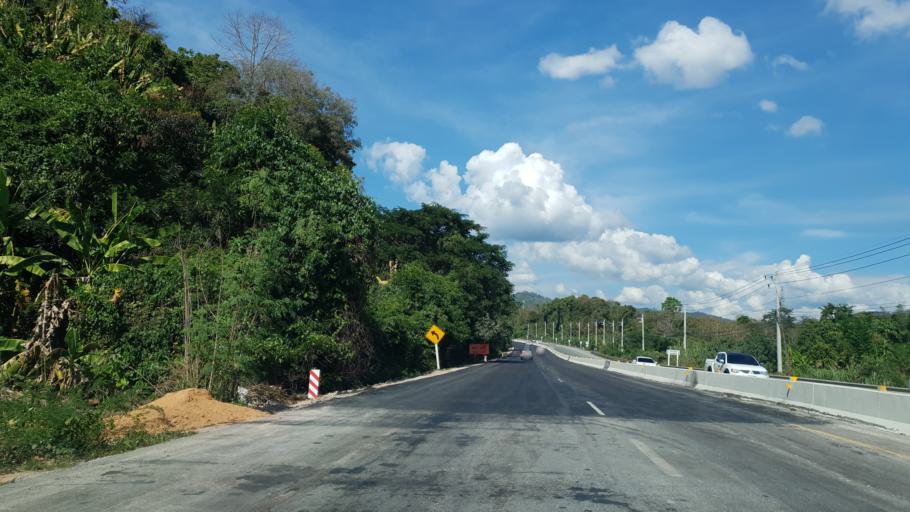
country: TH
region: Uttaradit
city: Uttaradit
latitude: 17.7524
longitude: 100.1342
